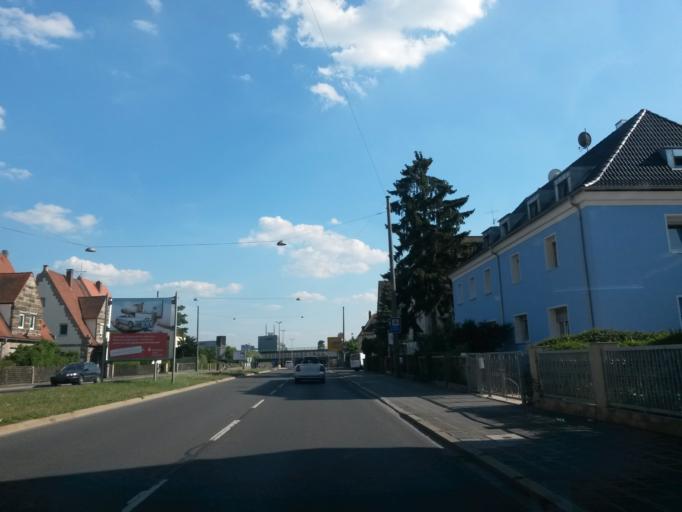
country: DE
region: Bavaria
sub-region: Regierungsbezirk Mittelfranken
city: Furth
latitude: 49.4544
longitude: 10.9889
